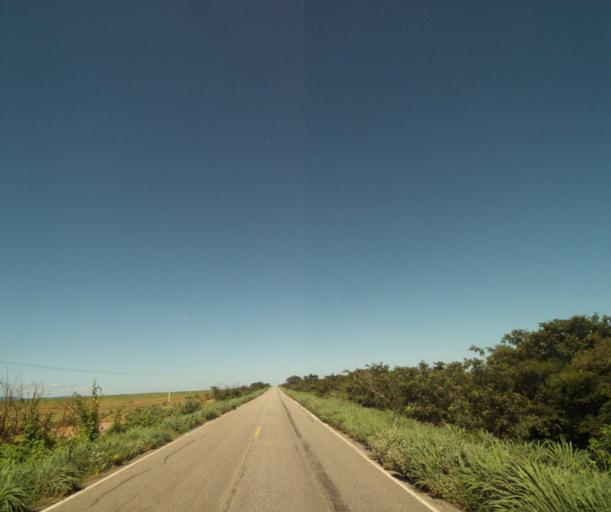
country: BR
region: Bahia
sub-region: Palmas De Monte Alto
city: Palmas de Monte Alto
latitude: -14.2705
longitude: -43.4171
